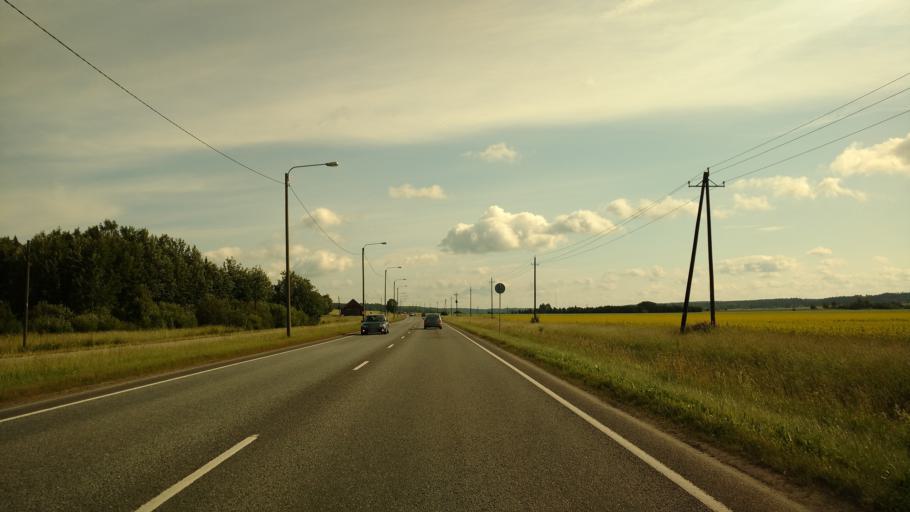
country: FI
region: Varsinais-Suomi
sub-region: Salo
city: Salo
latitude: 60.4047
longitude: 23.1502
